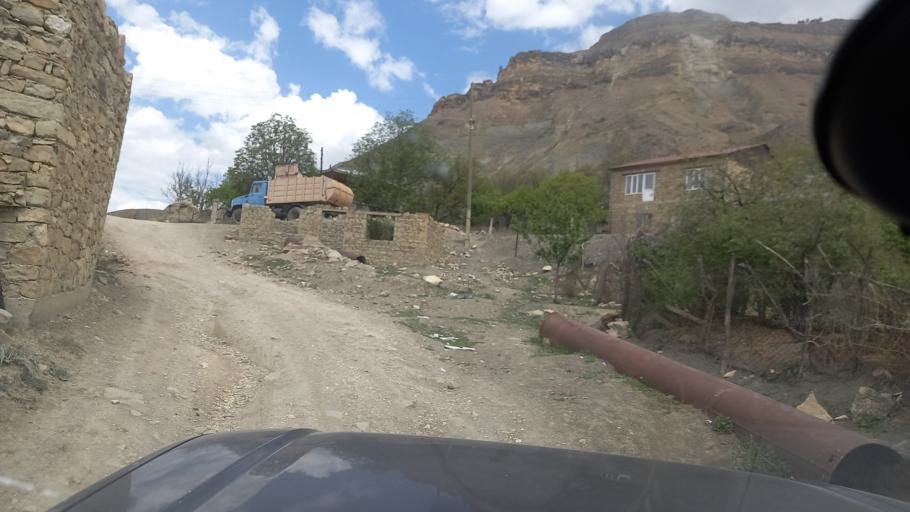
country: RU
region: Dagestan
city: Gunib
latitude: 42.3655
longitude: 46.9709
